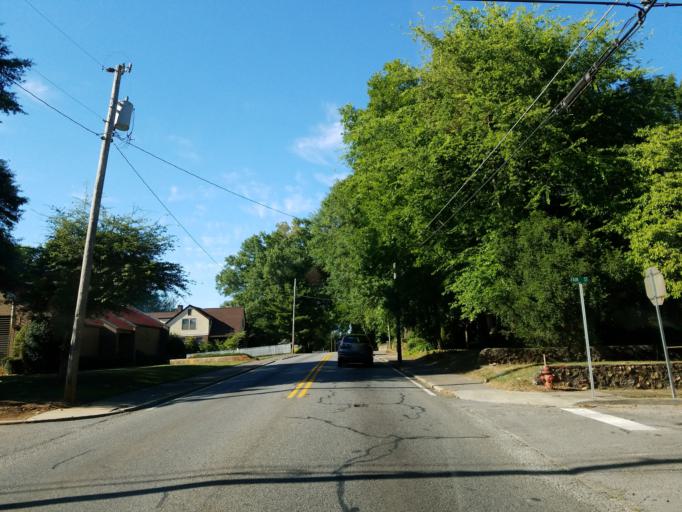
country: US
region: Georgia
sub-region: Gordon County
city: Calhoun
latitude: 34.5075
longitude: -84.9502
